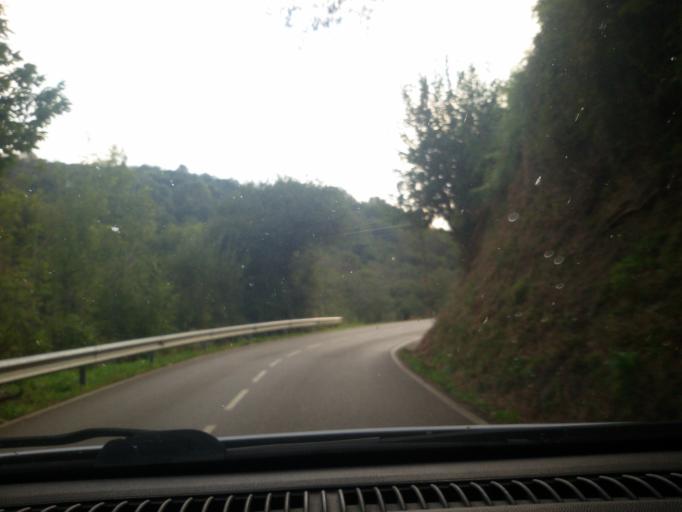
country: ES
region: Asturias
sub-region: Province of Asturias
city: Bimenes
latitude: 43.3361
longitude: -5.5793
